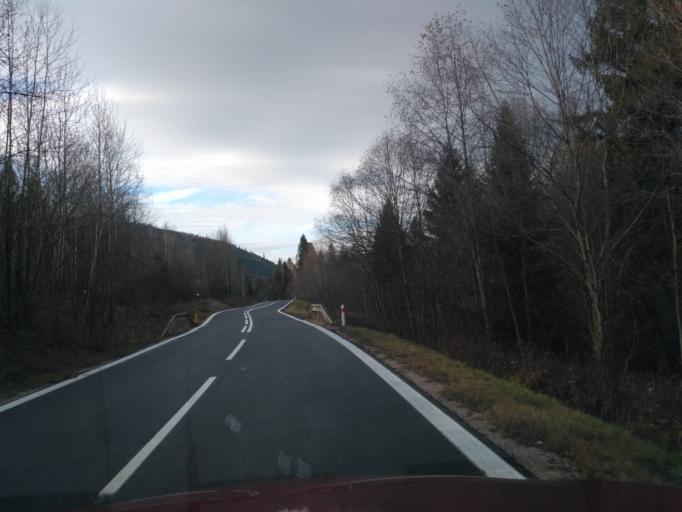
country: SK
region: Kosicky
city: Spisska Nova Ves
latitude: 48.8140
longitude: 20.6692
